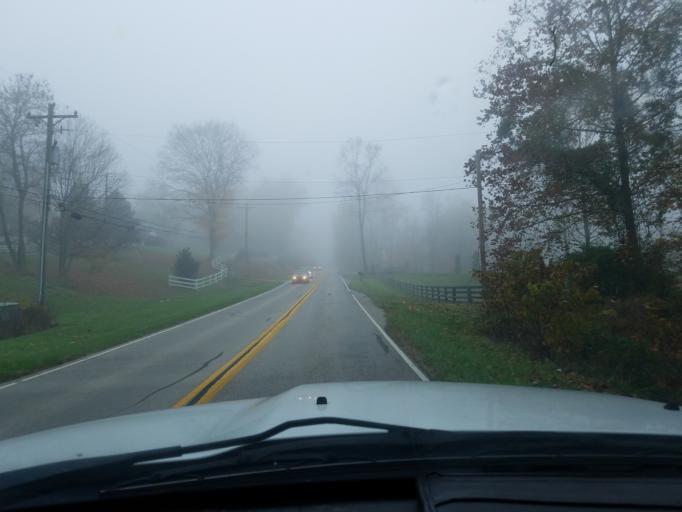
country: US
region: Indiana
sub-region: Floyd County
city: Galena
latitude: 38.3283
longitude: -85.8842
